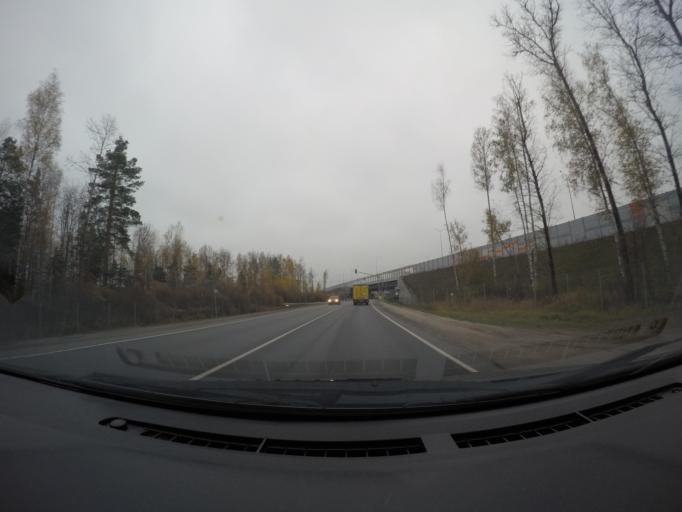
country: RU
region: Moskovskaya
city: Malyshevo
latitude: 55.5383
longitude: 38.4054
